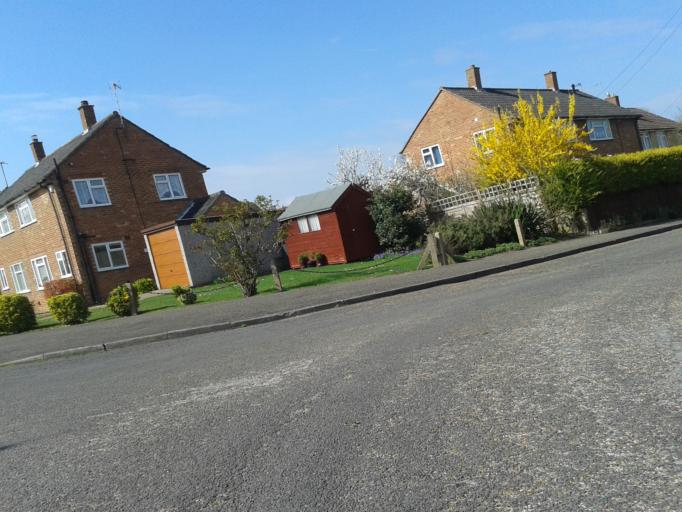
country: GB
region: England
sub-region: Cambridgeshire
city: Sawston
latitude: 52.1534
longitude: 0.1413
